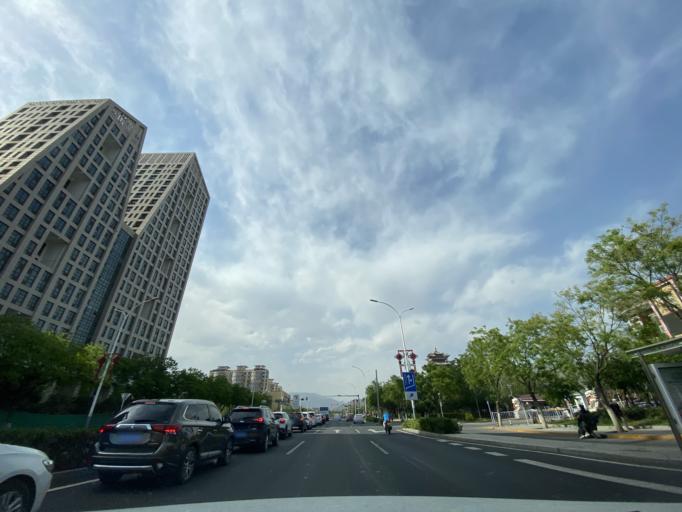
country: CN
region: Beijing
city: Dayu
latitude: 39.9422
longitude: 116.1015
